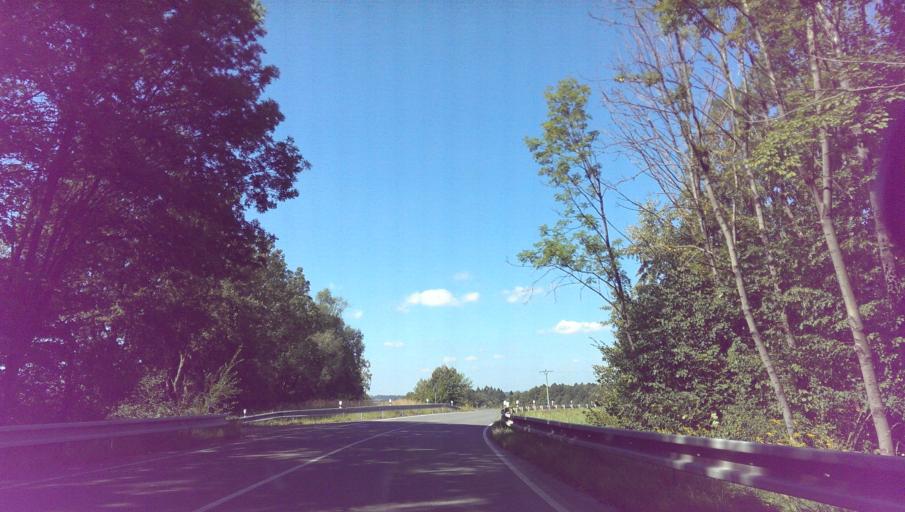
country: CZ
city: Staric
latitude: 49.6579
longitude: 18.2605
